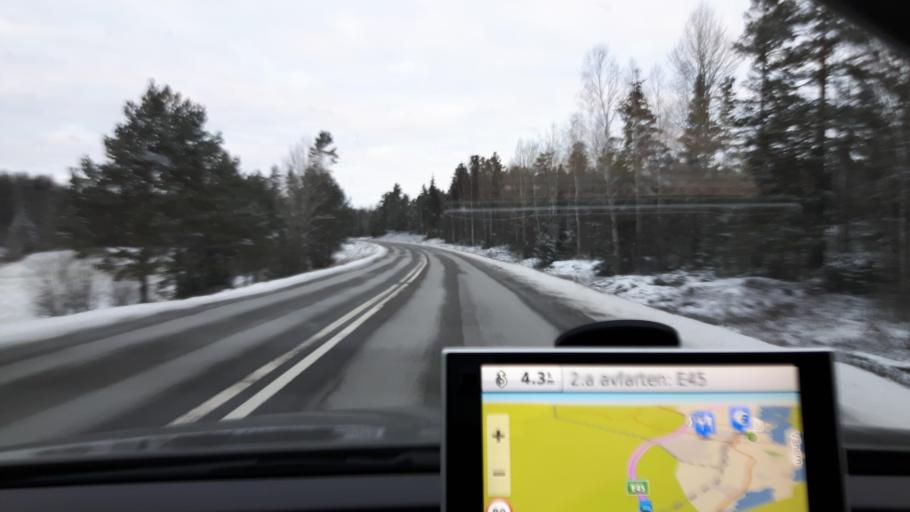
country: SE
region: Vaestra Goetaland
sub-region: Amals Kommun
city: Amal
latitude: 59.0198
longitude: 12.6866
